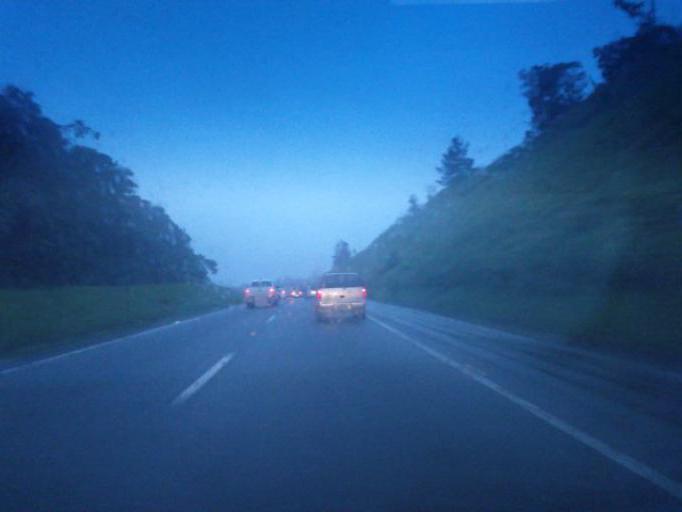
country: BR
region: Sao Paulo
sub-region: Juquitiba
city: Juquitiba
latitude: -23.9651
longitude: -47.1268
